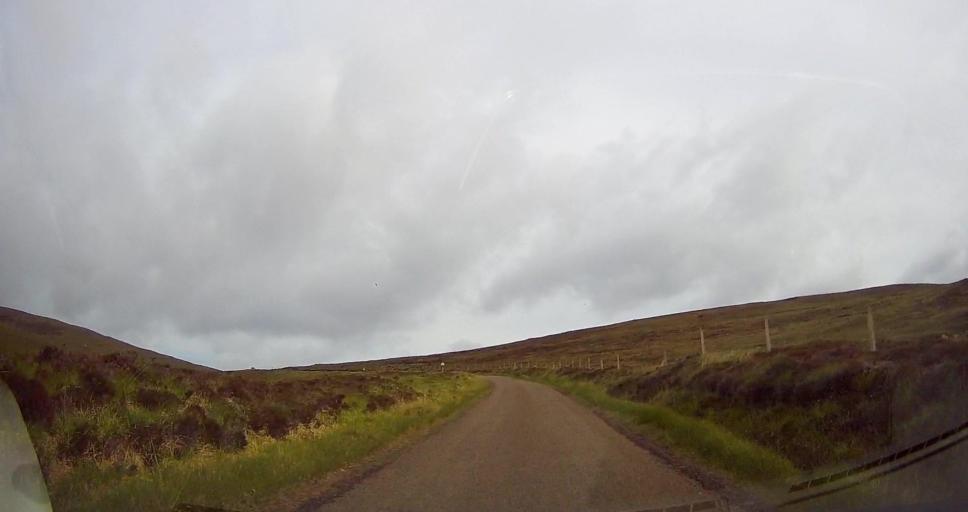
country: GB
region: Scotland
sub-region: Orkney Islands
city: Stromness
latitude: 58.8761
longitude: -3.2470
